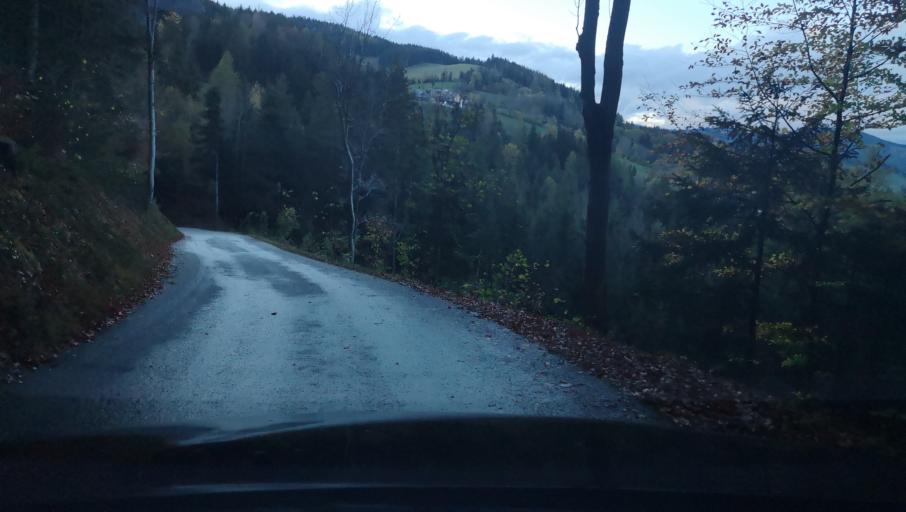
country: AT
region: Styria
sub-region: Politischer Bezirk Weiz
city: Birkfeld
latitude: 47.3348
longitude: 15.6694
